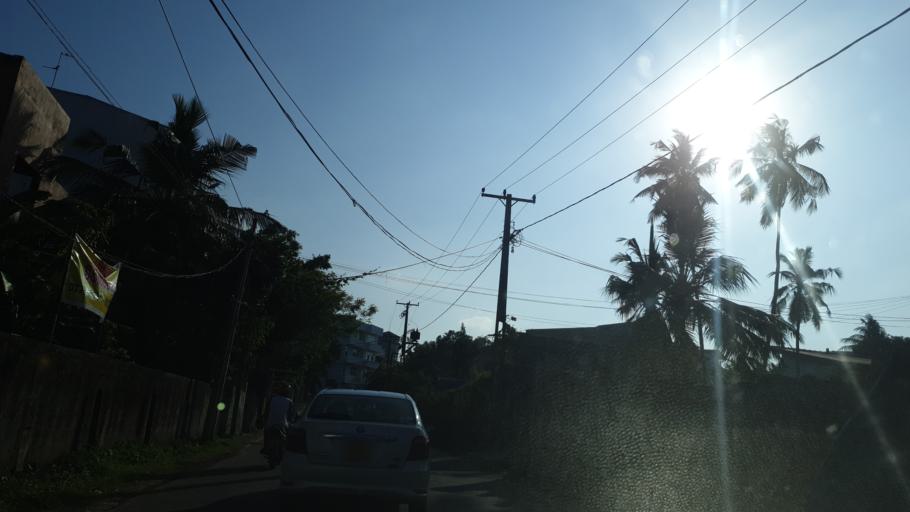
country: LK
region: Western
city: Sri Jayewardenepura Kotte
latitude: 6.8703
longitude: 79.9128
